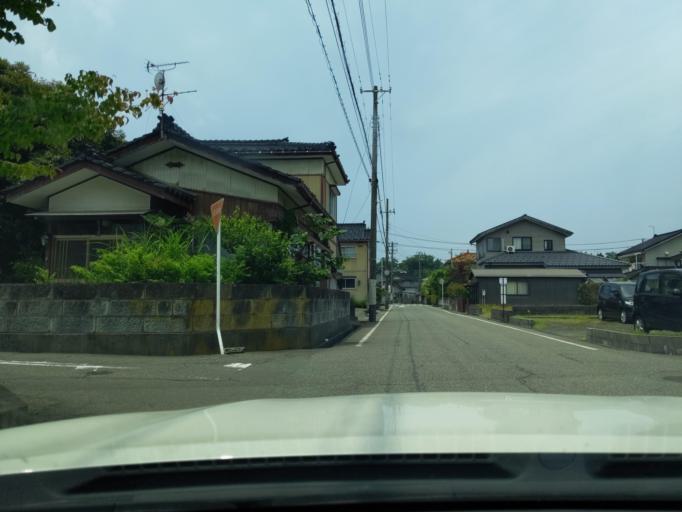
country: JP
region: Niigata
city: Kashiwazaki
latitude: 37.3534
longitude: 138.5425
